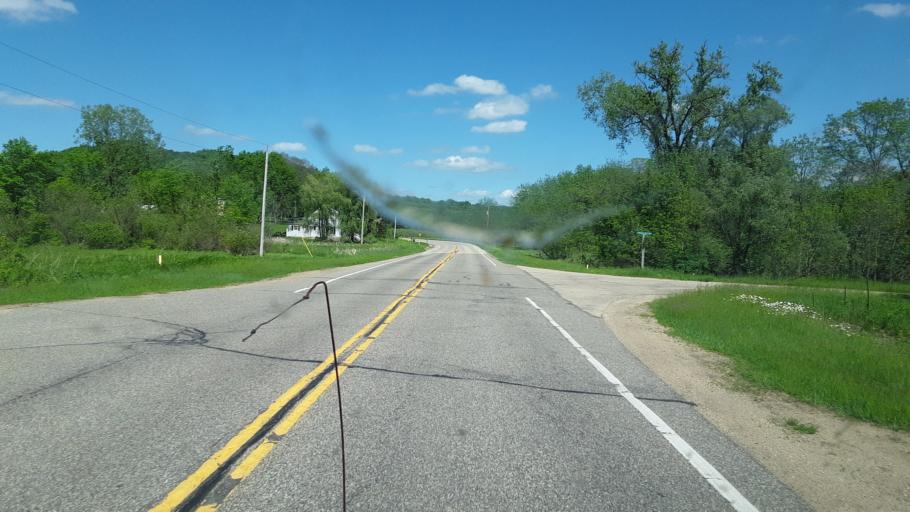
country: US
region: Wisconsin
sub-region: Richland County
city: Richland Center
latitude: 43.4573
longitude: -90.2175
